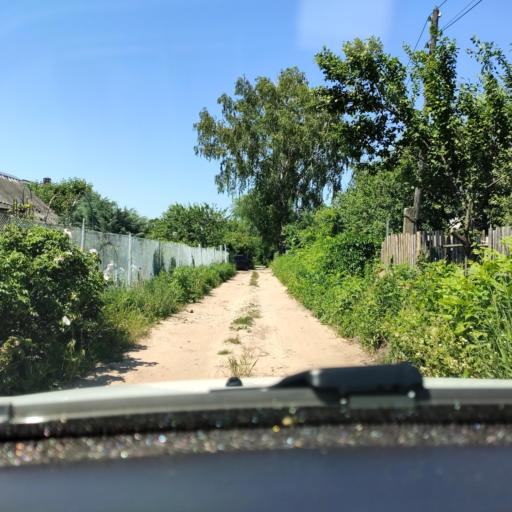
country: RU
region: Voronezj
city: Shilovo
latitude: 51.5935
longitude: 39.1445
